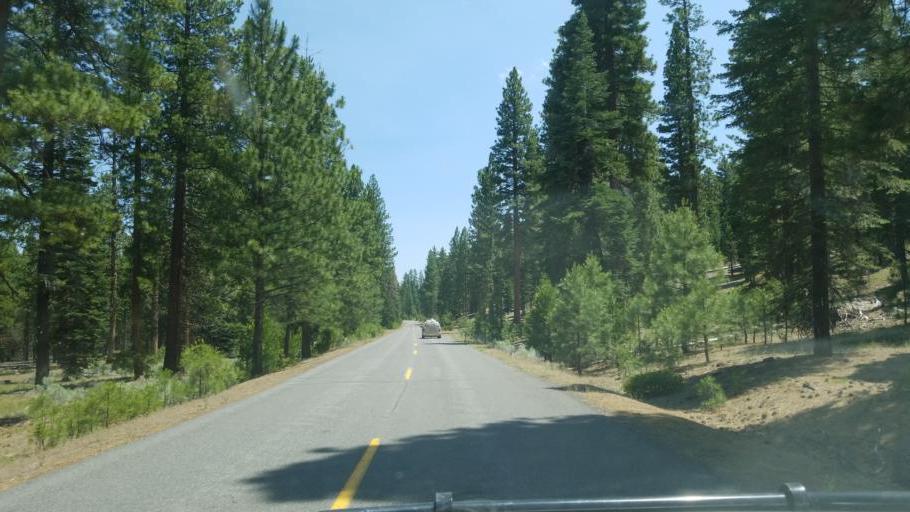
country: US
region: California
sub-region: Lassen County
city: Susanville
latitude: 40.5545
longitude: -120.8243
